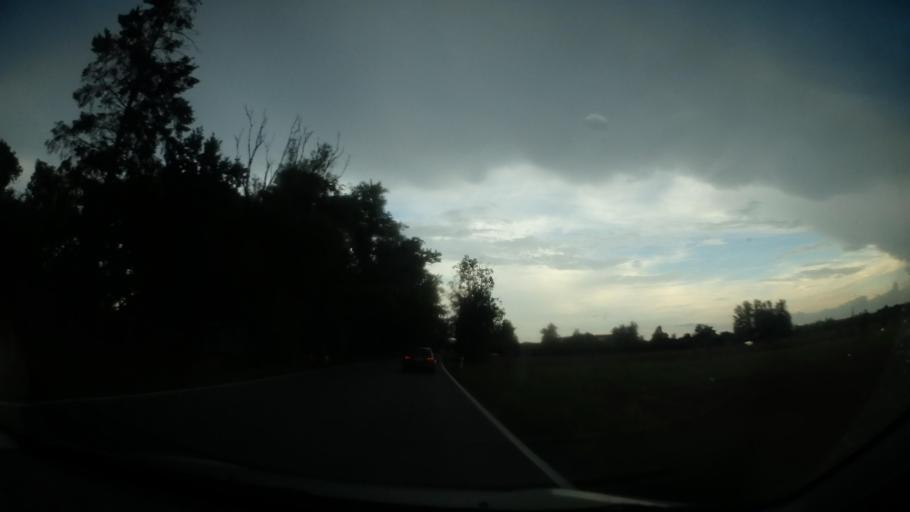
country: CZ
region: Olomoucky
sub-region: Okres Olomouc
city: Olomouc
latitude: 49.6176
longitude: 17.2521
